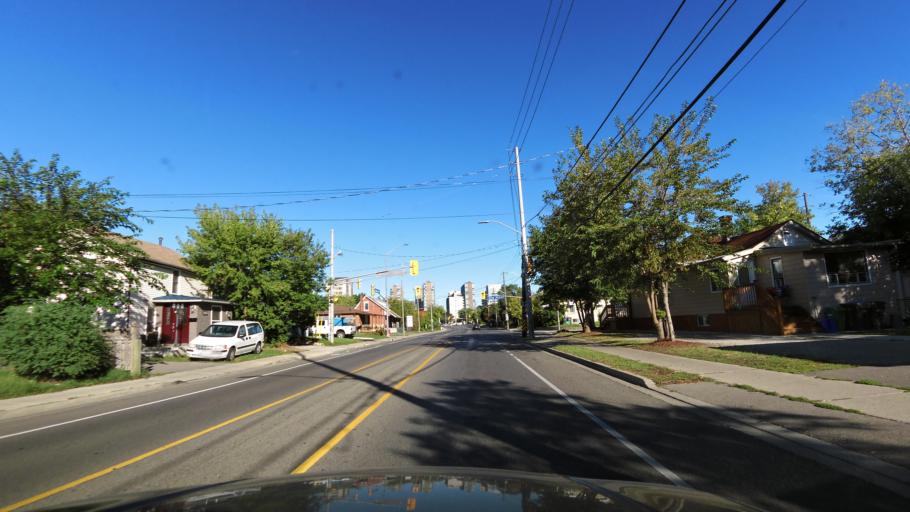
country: CA
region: Ontario
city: Mississauga
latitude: 43.5756
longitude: -79.6163
